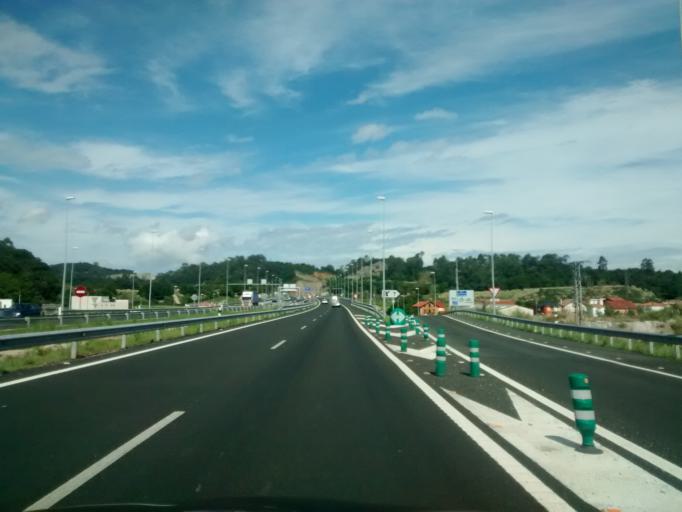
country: ES
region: Cantabria
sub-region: Provincia de Cantabria
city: Camargo
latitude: 43.4022
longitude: -3.8694
